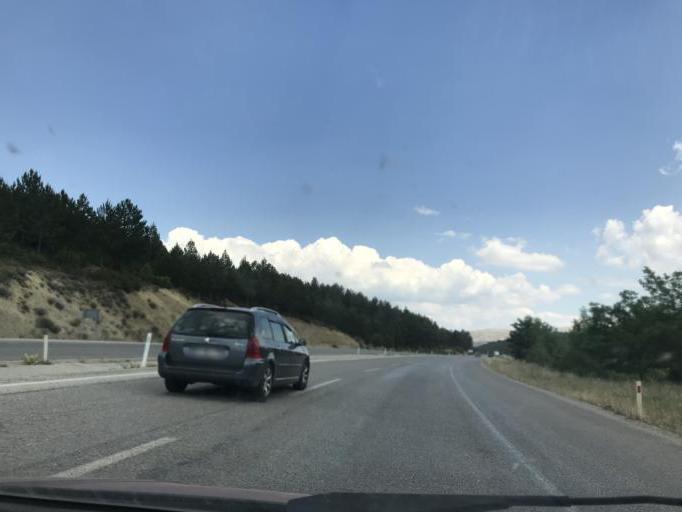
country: TR
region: Denizli
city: Tavas
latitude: 37.6142
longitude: 29.1466
